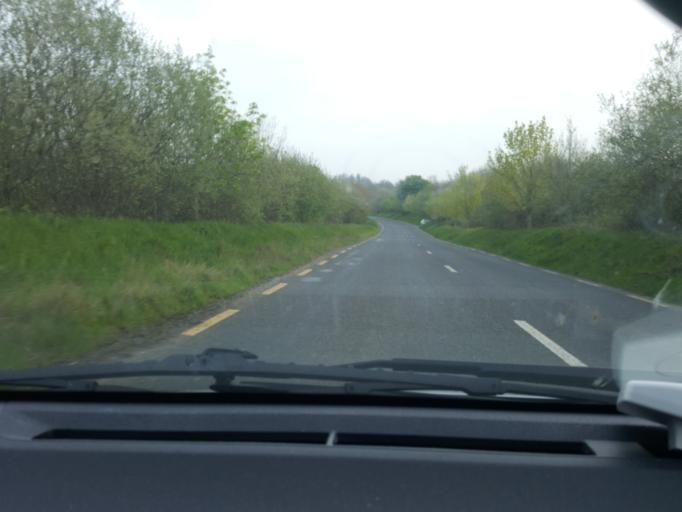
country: IE
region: Munster
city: Cahir
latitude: 52.3911
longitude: -7.9113
